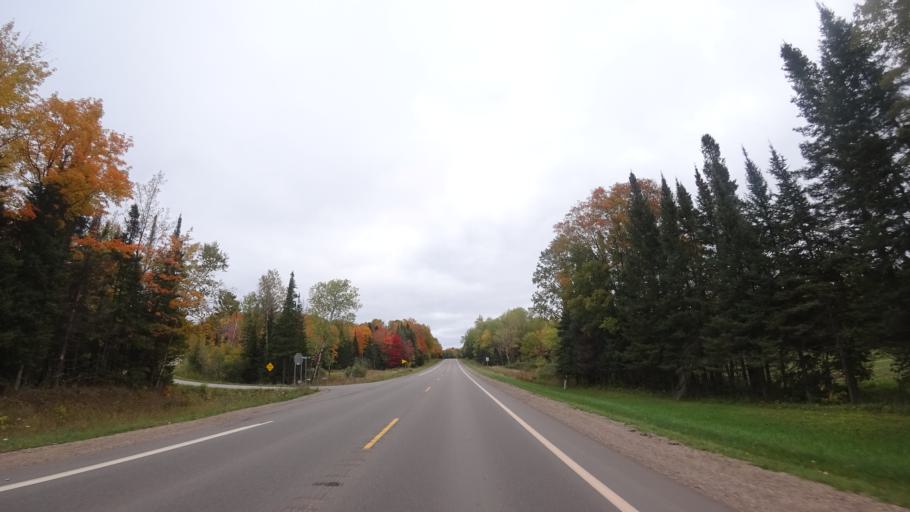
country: US
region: Michigan
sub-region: Iron County
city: Crystal Falls
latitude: 46.1713
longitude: -88.0631
